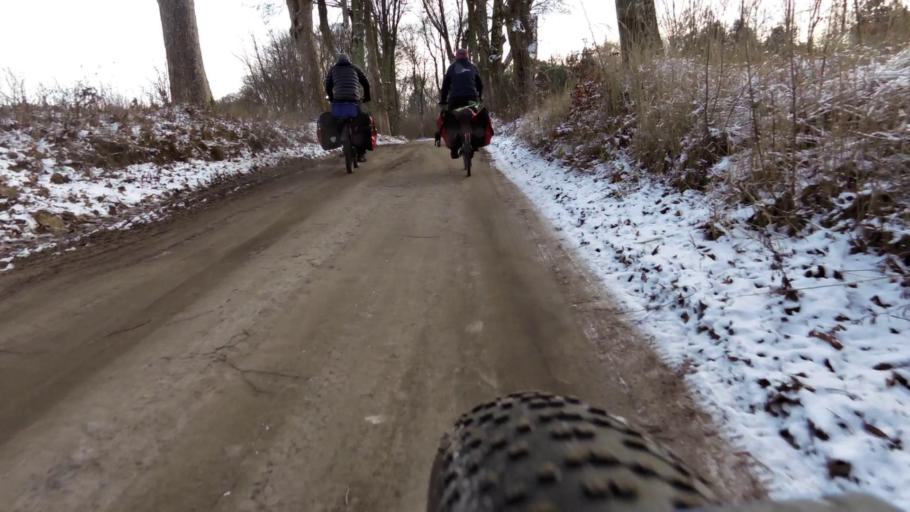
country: PL
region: West Pomeranian Voivodeship
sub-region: Powiat walecki
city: Walcz
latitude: 53.2651
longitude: 16.3122
